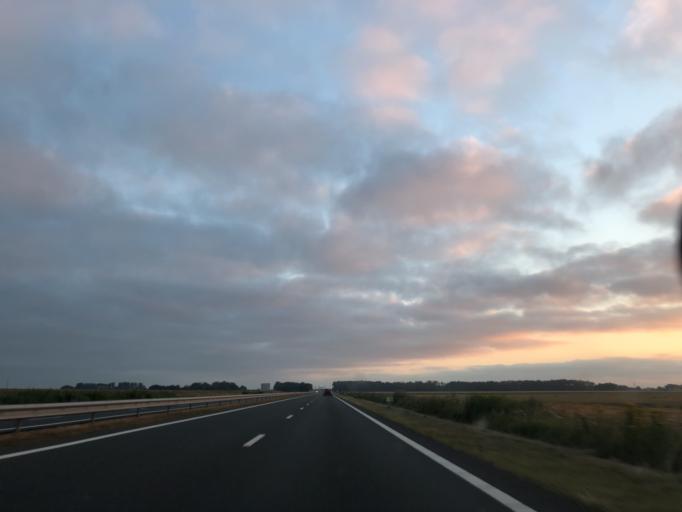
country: NL
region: Groningen
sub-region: Gemeente Veendam
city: Veendam
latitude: 53.1487
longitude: 6.8971
